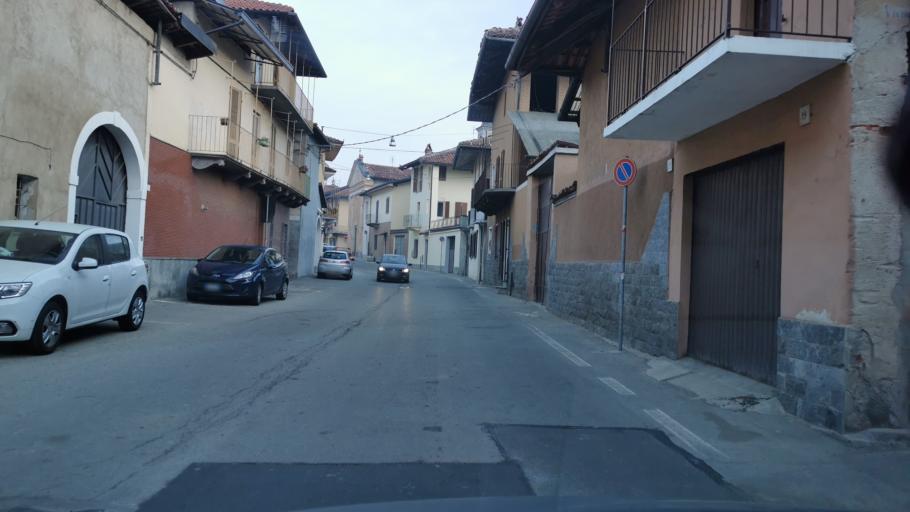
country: IT
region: Piedmont
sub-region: Provincia di Torino
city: San Giorgio Canavese
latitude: 45.3335
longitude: 7.7952
